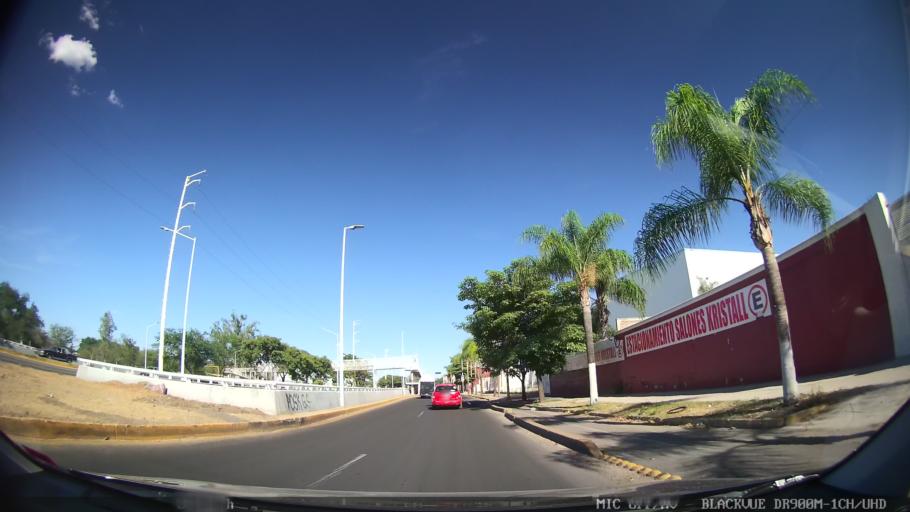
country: MX
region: Jalisco
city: Tlaquepaque
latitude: 20.7160
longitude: -103.3075
